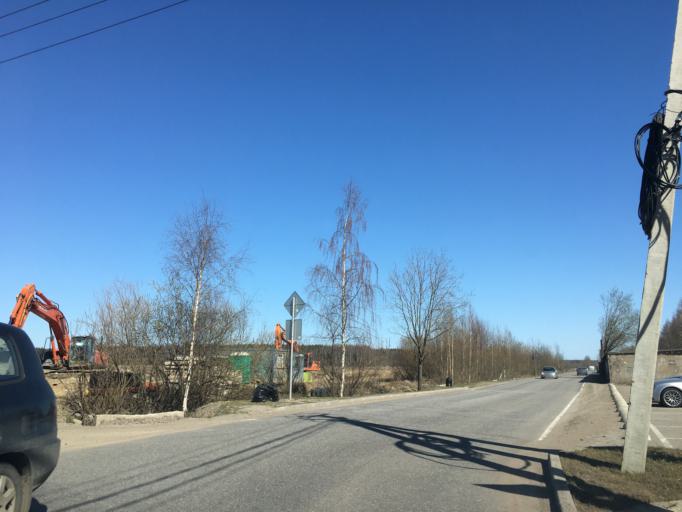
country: RU
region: Leningrad
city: Yanino Vtoroye
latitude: 59.9518
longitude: 30.5584
